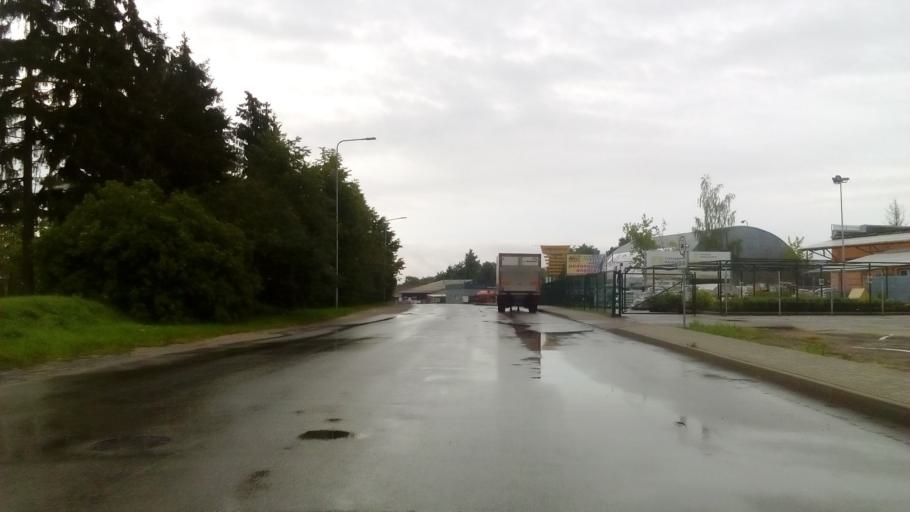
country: LT
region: Alytaus apskritis
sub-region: Alytus
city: Alytus
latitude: 54.3914
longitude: 24.0372
